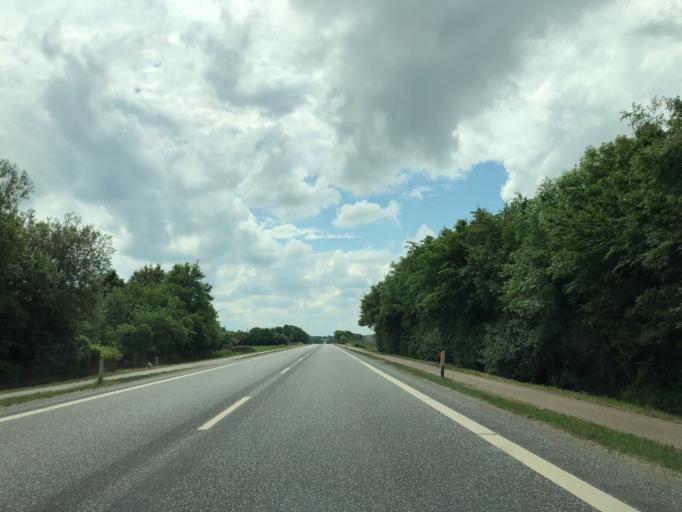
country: DK
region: Central Jutland
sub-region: Struer Kommune
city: Struer
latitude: 56.4701
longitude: 8.5869
